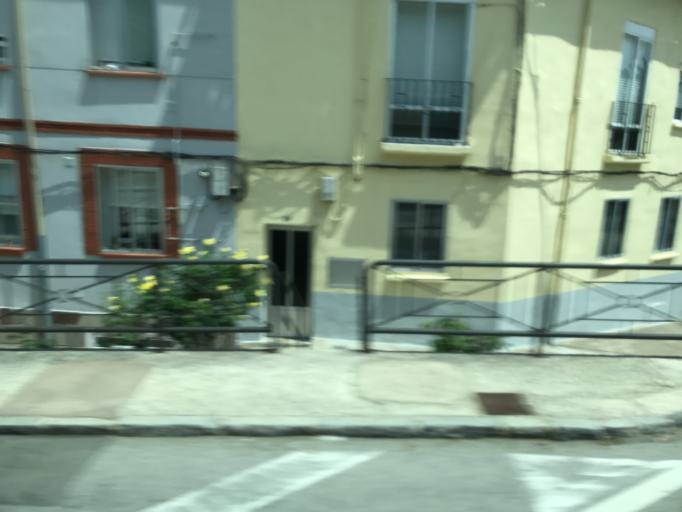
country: ES
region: Castille and Leon
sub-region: Provincia de Burgos
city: Burgos
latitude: 42.3268
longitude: -3.7009
